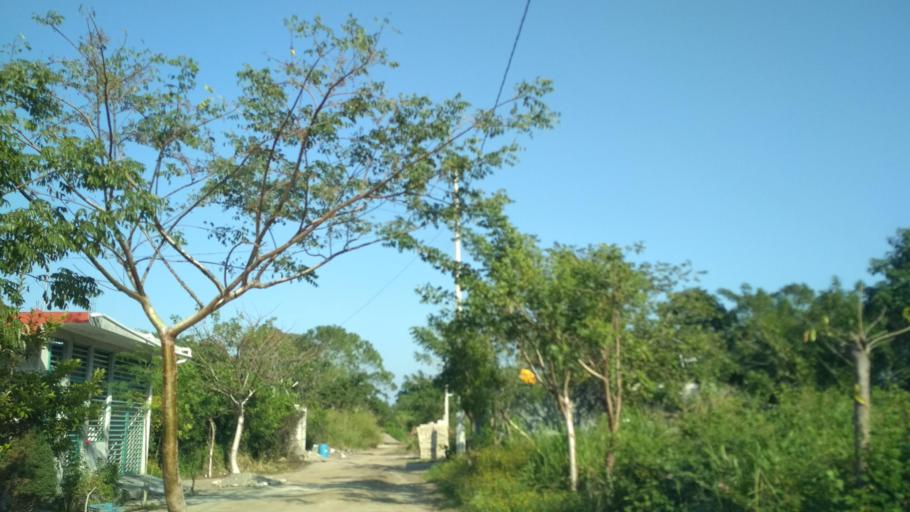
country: MX
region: Veracruz
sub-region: Martinez de la Torre
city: El Progreso
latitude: 20.0876
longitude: -97.0208
